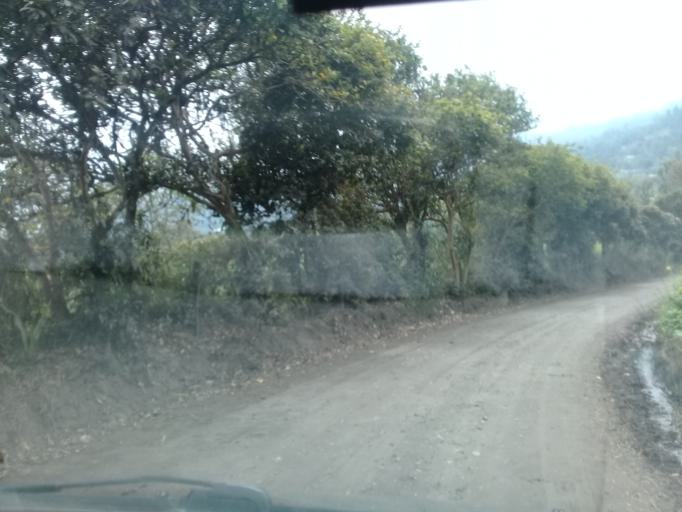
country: CO
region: Cundinamarca
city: Une
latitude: 4.4086
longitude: -73.9901
